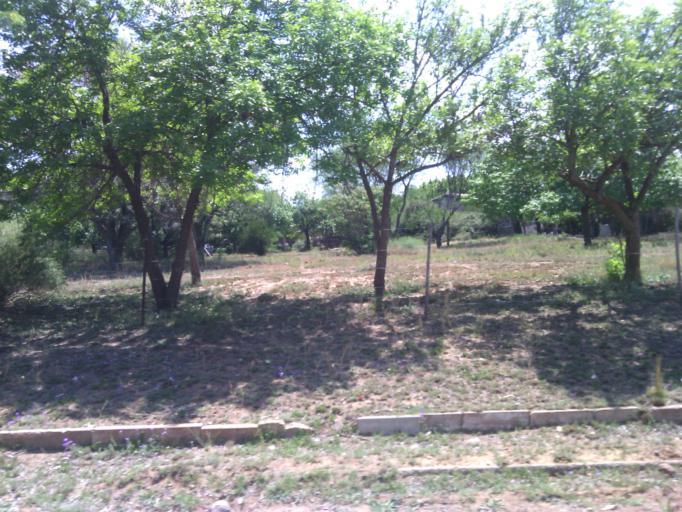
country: ZA
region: Orange Free State
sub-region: Xhariep District Municipality
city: Dewetsdorp
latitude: -29.5890
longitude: 26.6648
